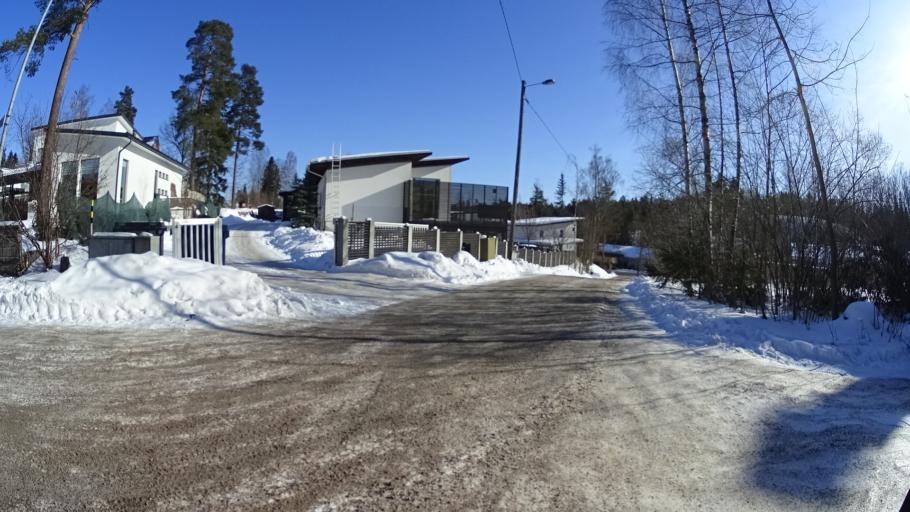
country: FI
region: Uusimaa
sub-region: Helsinki
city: Kauniainen
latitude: 60.2226
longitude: 24.6987
